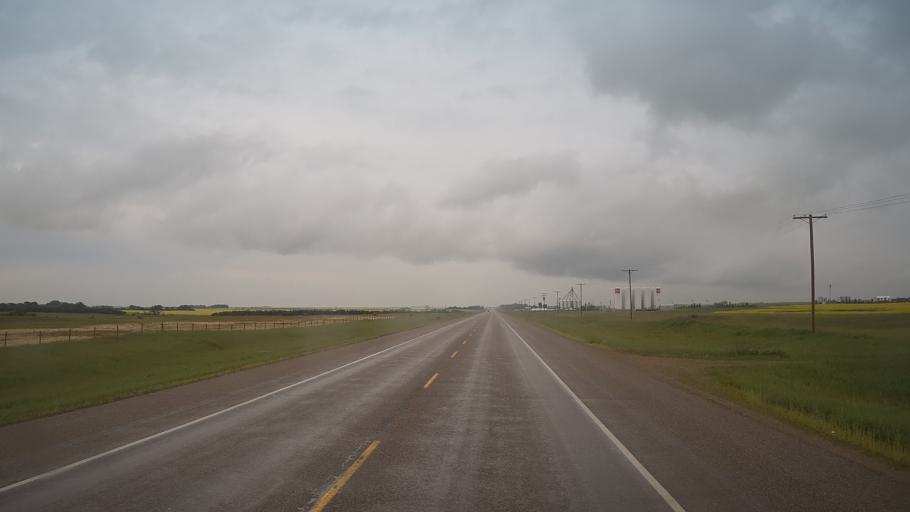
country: CA
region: Saskatchewan
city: Wilkie
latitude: 52.4057
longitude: -108.7414
